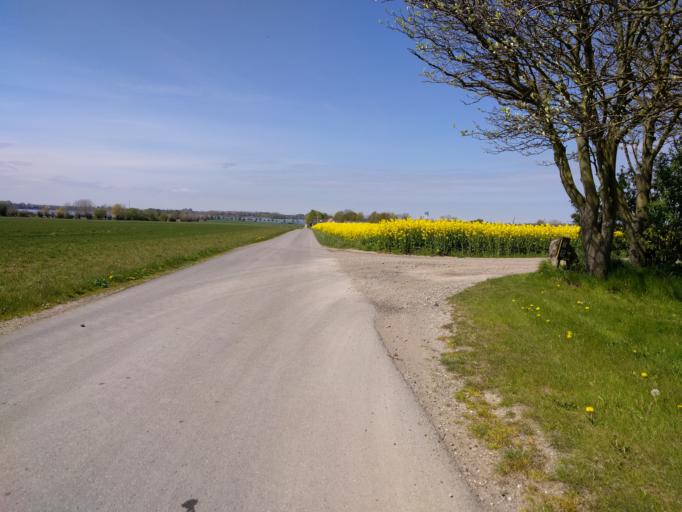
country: DK
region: South Denmark
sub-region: Kerteminde Kommune
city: Munkebo
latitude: 55.4452
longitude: 10.5945
